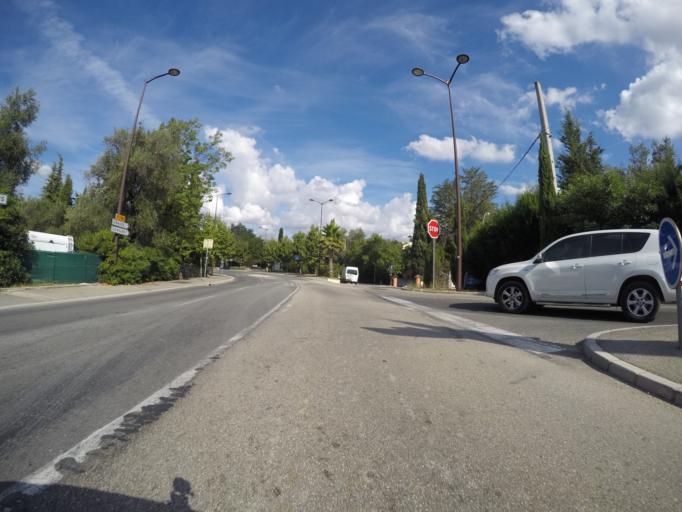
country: FR
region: Provence-Alpes-Cote d'Azur
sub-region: Departement des Alpes-Maritimes
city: Le Rouret
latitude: 43.6768
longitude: 7.0182
